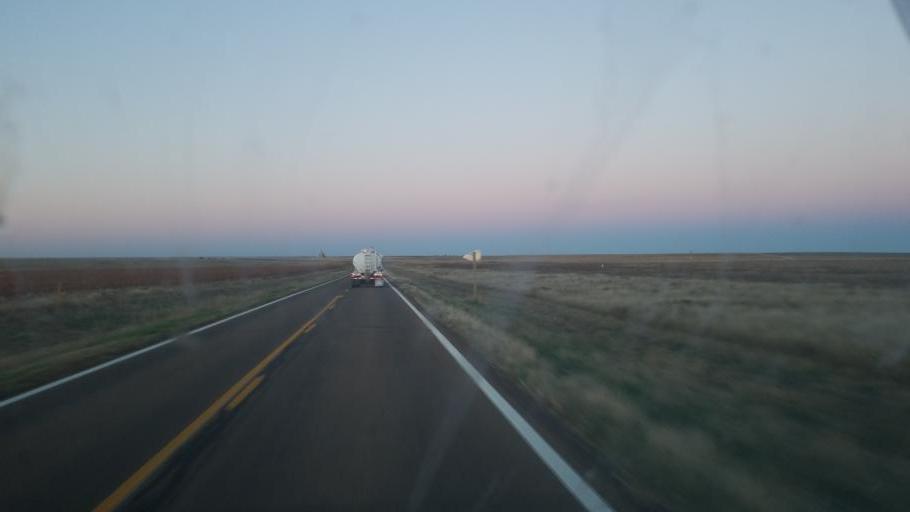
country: US
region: Kansas
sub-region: Wallace County
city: Sharon Springs
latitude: 38.9297
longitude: -101.5481
